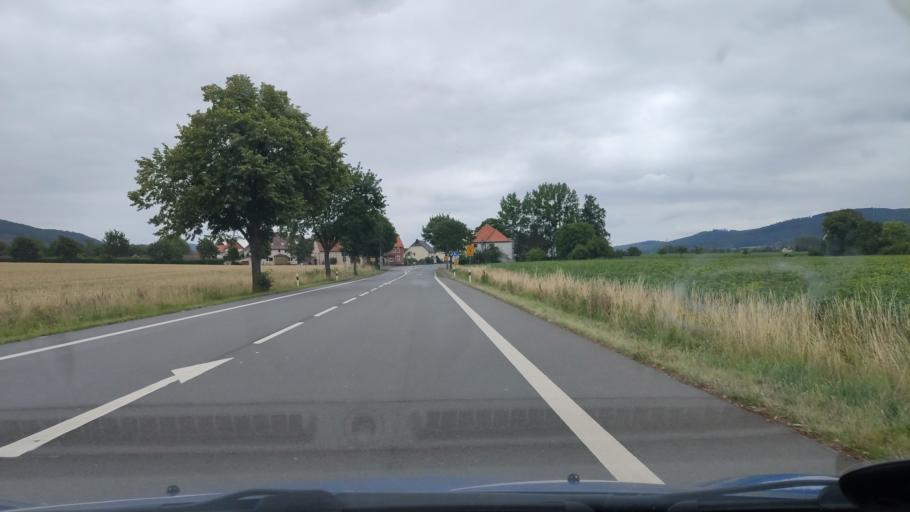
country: DE
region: Lower Saxony
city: Luerdissen
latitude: 51.9505
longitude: 9.6194
